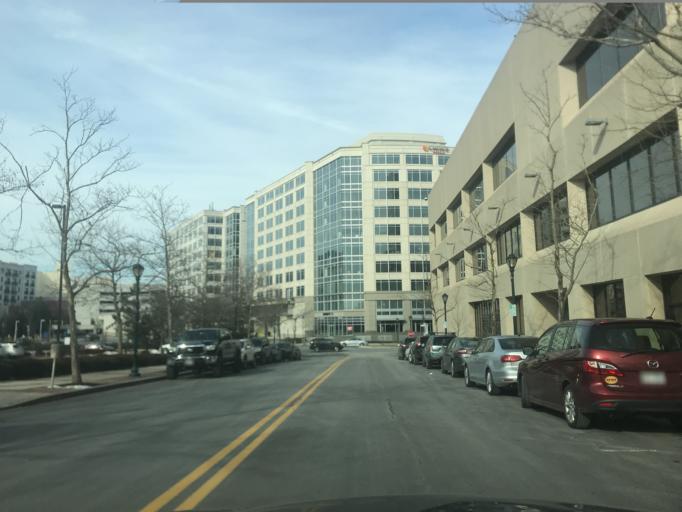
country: US
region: Maryland
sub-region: Montgomery County
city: Rockville
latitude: 39.0842
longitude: -77.1492
